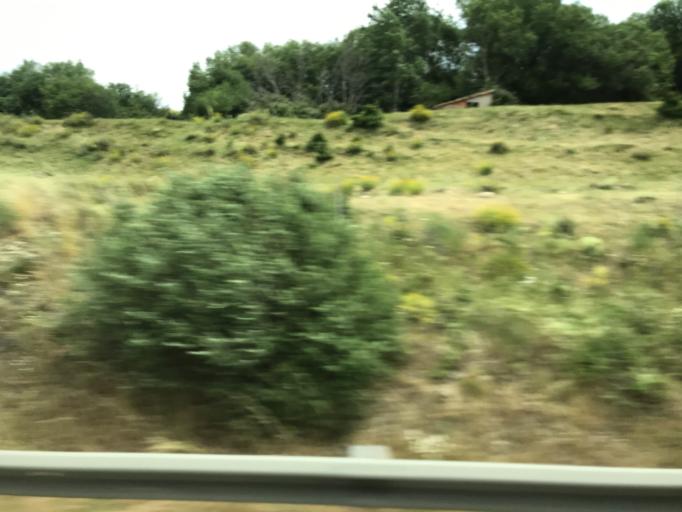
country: ES
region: Madrid
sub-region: Provincia de Madrid
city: Somosierra
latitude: 41.1728
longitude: -3.5793
